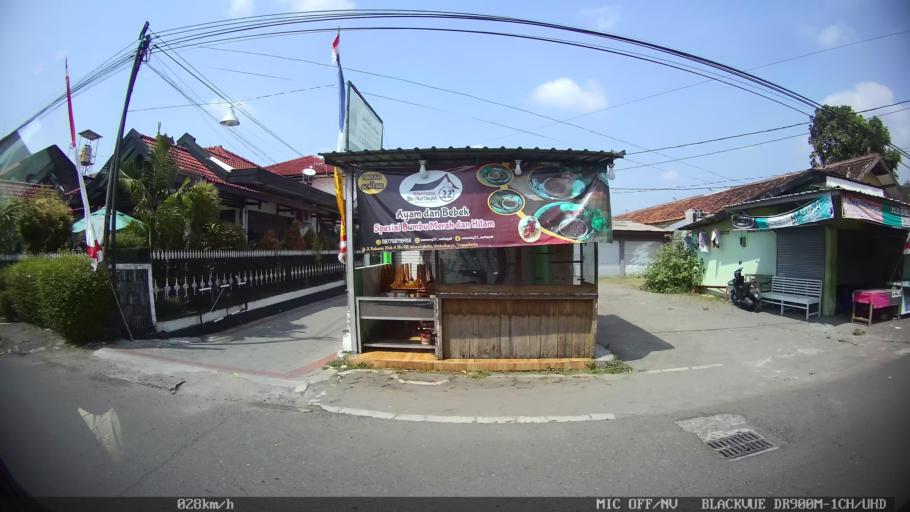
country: ID
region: Daerah Istimewa Yogyakarta
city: Yogyakarta
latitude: -7.8121
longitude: 110.3887
